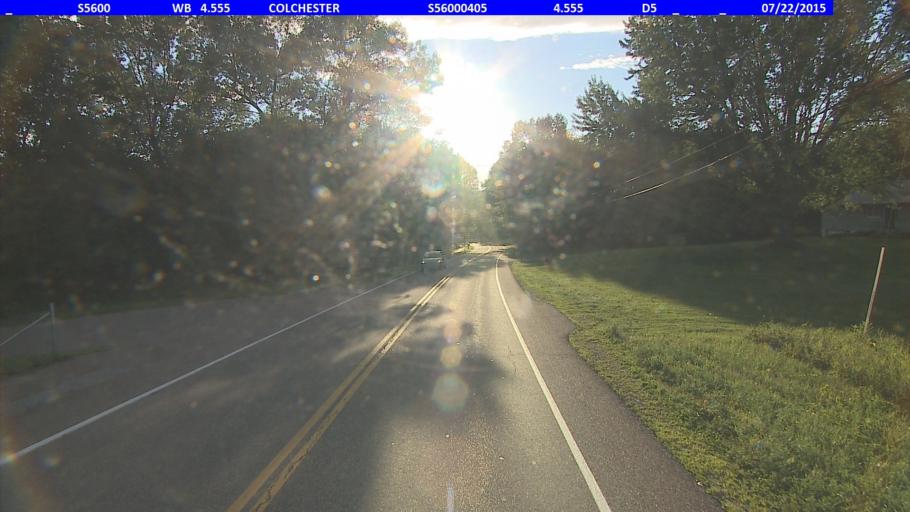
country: US
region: Vermont
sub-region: Chittenden County
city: Winooski
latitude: 44.5308
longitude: -73.1973
